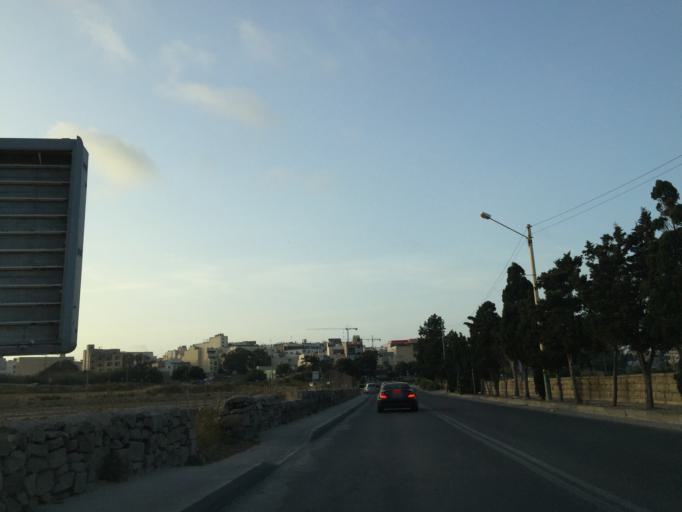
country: MT
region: Saint Paul's Bay
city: San Pawl il-Bahar
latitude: 35.9424
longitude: 14.4115
